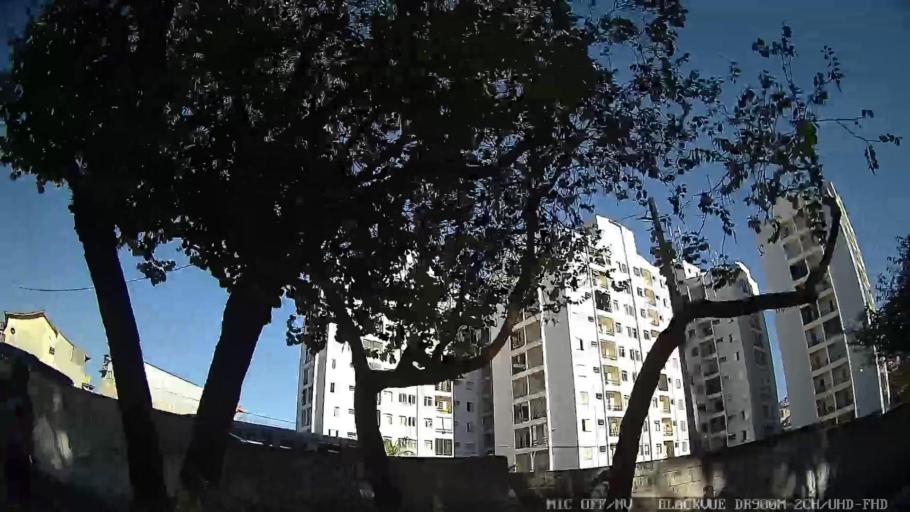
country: BR
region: Sao Paulo
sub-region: Guarulhos
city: Guarulhos
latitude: -23.5277
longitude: -46.5159
